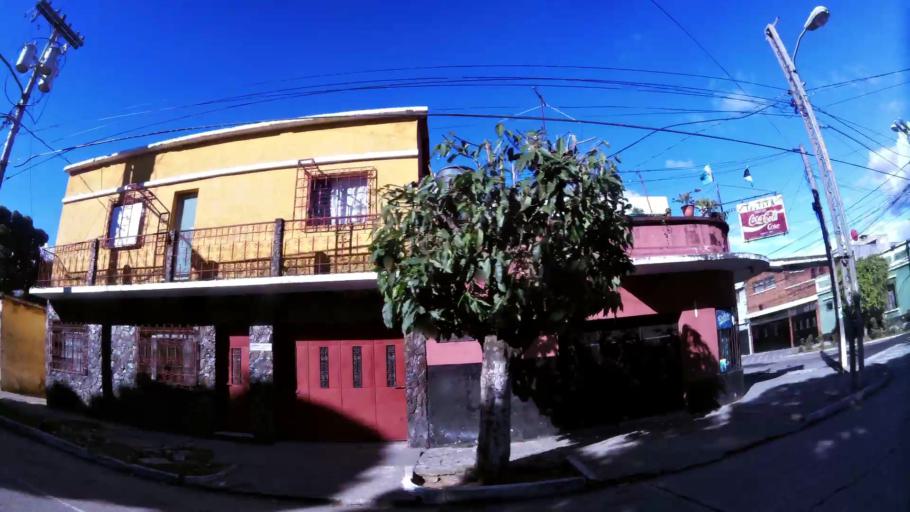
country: GT
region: Guatemala
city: Guatemala City
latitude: 14.6235
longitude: -90.5078
